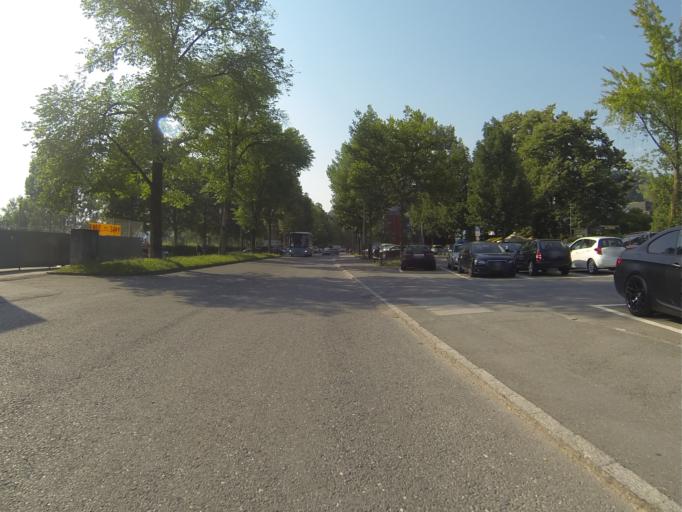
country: CH
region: Lucerne
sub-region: Lucerne-Land District
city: Adligenswil
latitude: 47.0508
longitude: 8.3367
